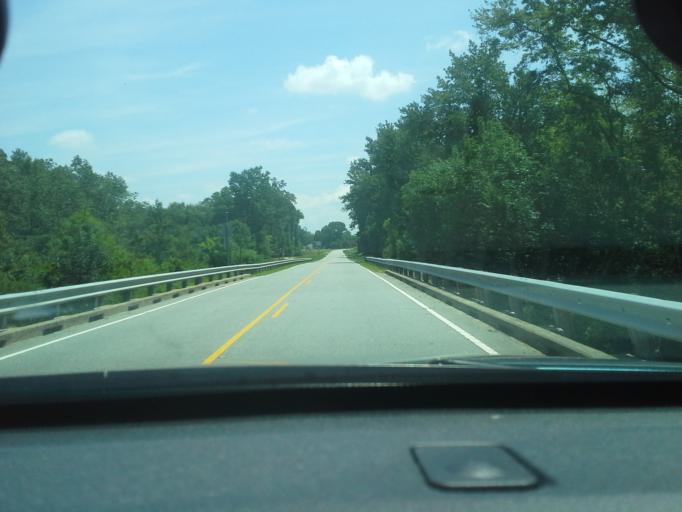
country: US
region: North Carolina
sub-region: Chowan County
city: Edenton
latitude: 35.9301
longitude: -76.6100
